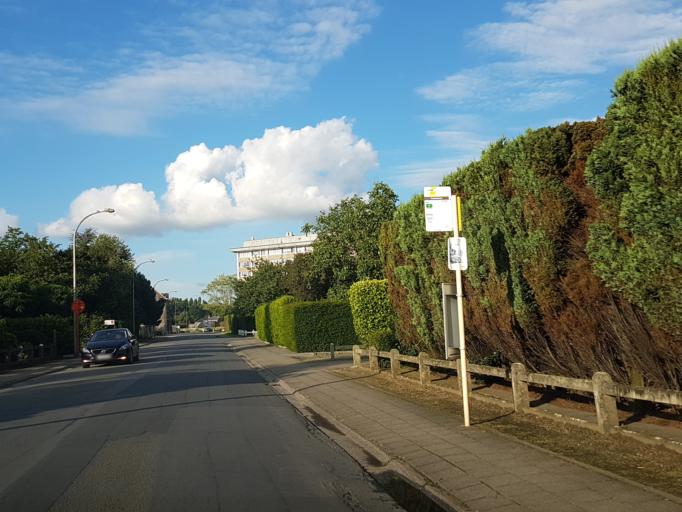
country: BE
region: Flanders
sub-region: Provincie Oost-Vlaanderen
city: Aalst
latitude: 50.9503
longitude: 4.0637
